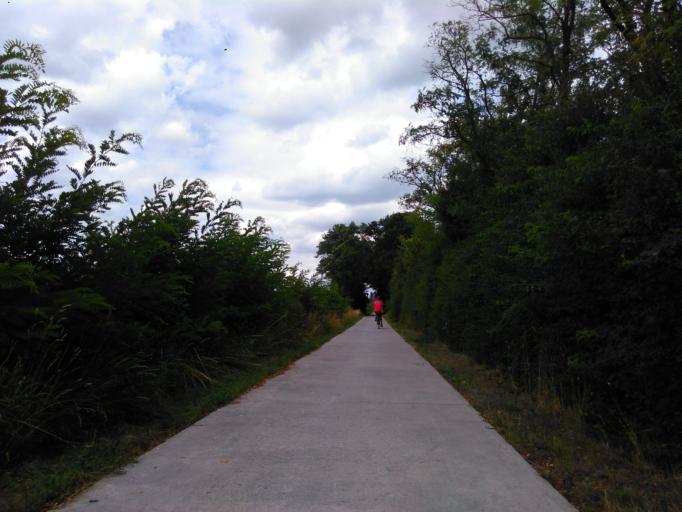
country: LU
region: Grevenmacher
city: Gonderange
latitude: 49.6852
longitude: 6.2499
